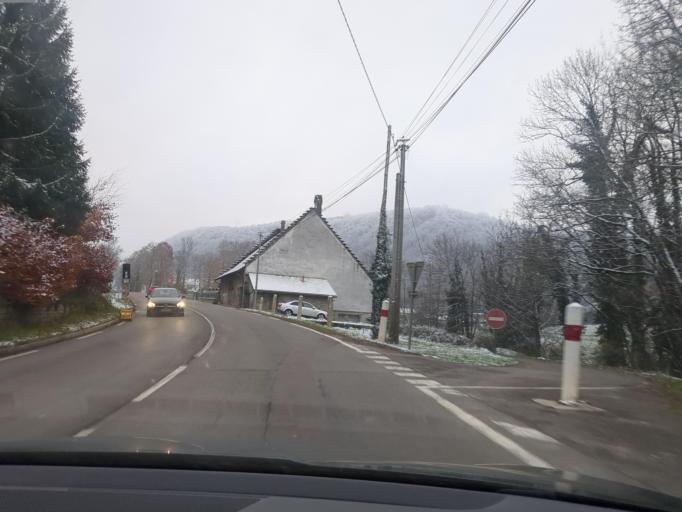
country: FR
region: Franche-Comte
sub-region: Departement du Jura
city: Perrigny
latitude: 46.6413
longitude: 5.6017
